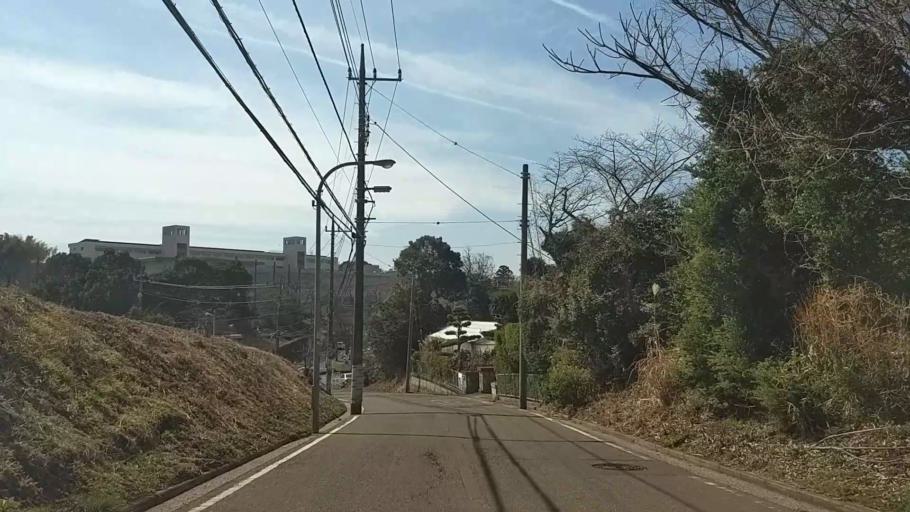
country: JP
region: Kanagawa
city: Fujisawa
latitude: 35.3934
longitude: 139.5182
